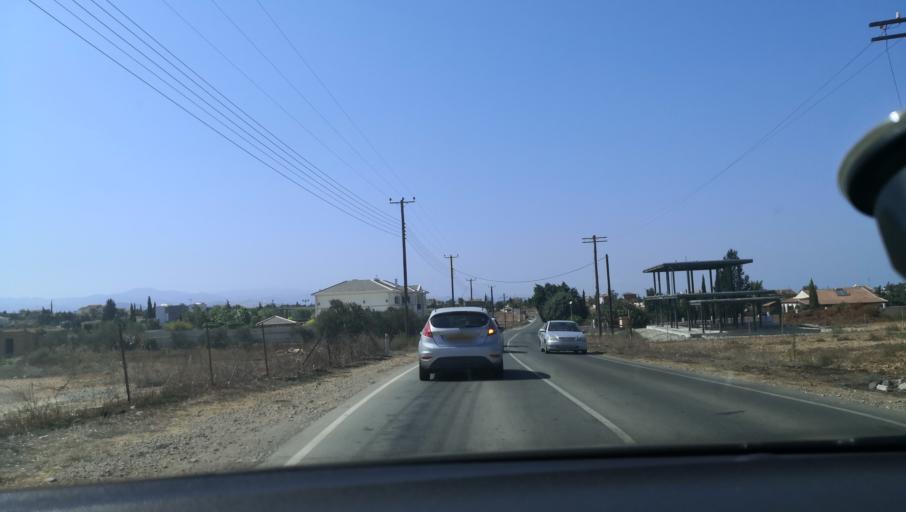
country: CY
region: Lefkosia
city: Pano Deftera
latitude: 35.1182
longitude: 33.2370
